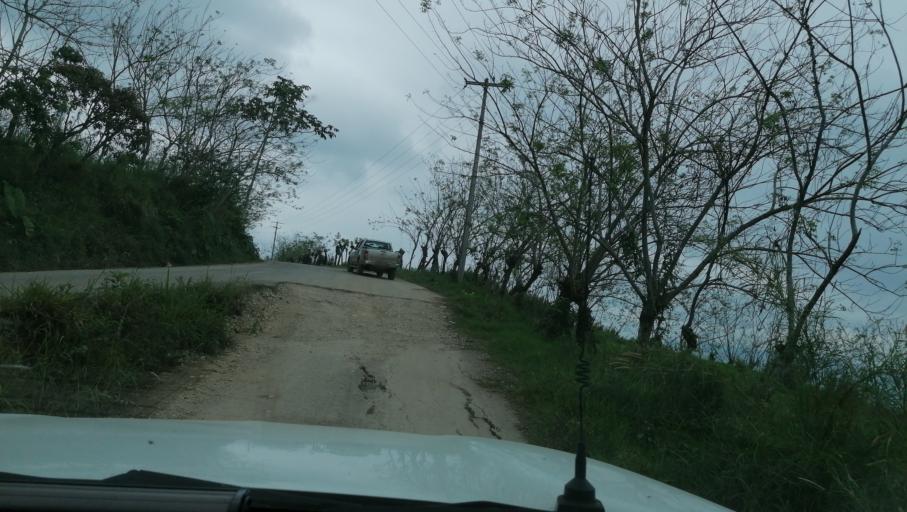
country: MX
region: Chiapas
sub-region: Ocotepec
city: San Pablo Huacano
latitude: 17.2694
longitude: -93.2634
